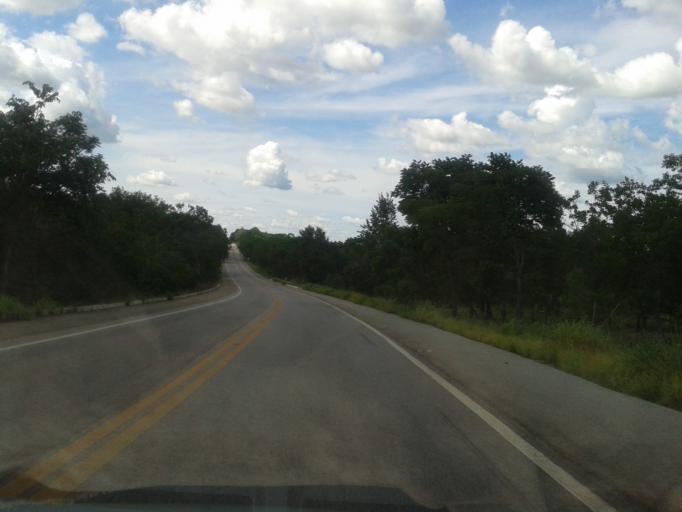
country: BR
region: Goias
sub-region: Itapuranga
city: Itapuranga
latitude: -15.5435
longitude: -50.2888
